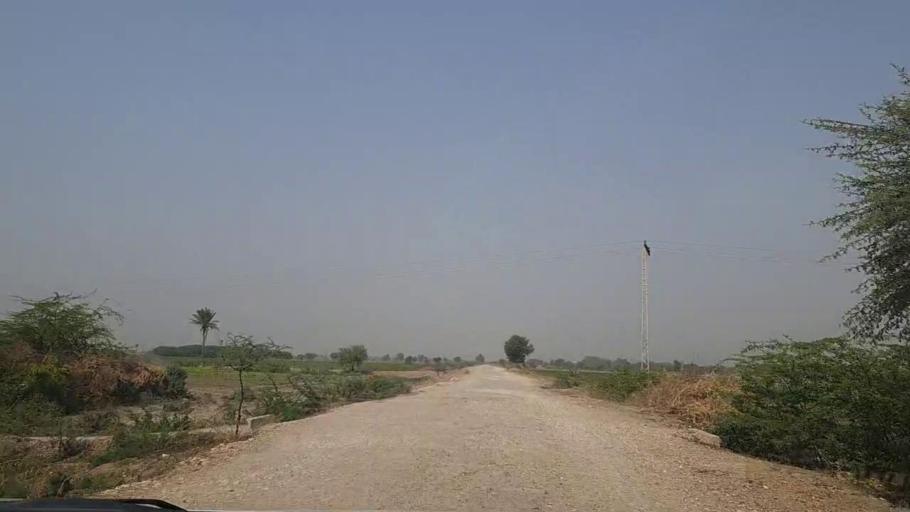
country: PK
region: Sindh
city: Mirpur Khas
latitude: 25.5951
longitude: 69.2010
